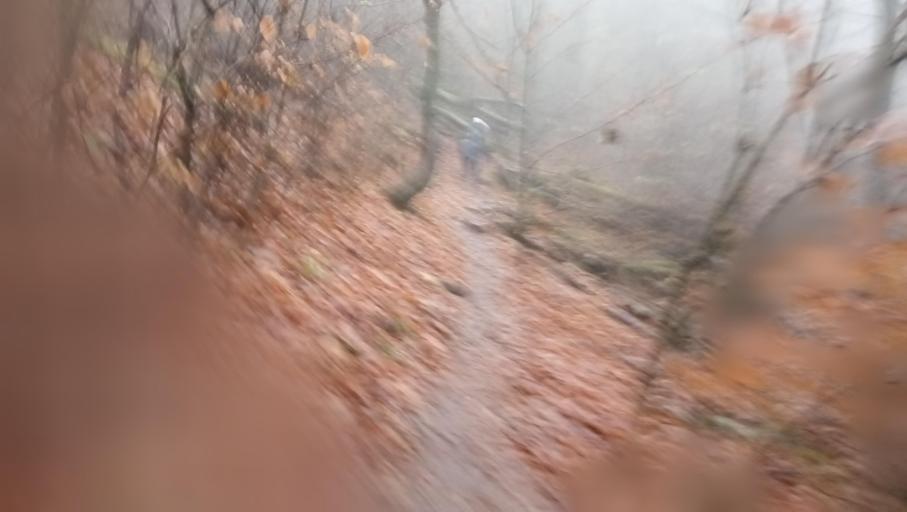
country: HU
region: Pest
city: Pilisszentkereszt
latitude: 47.7172
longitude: 18.8985
